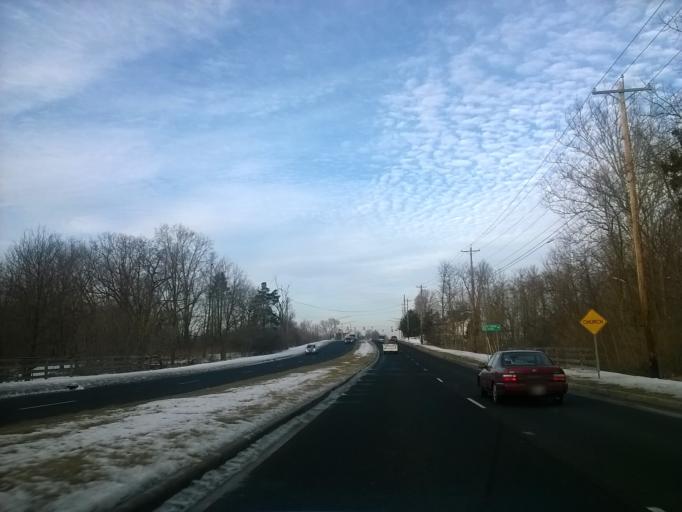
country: US
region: Indiana
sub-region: Hamilton County
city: Carmel
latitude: 40.0003
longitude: -86.0859
